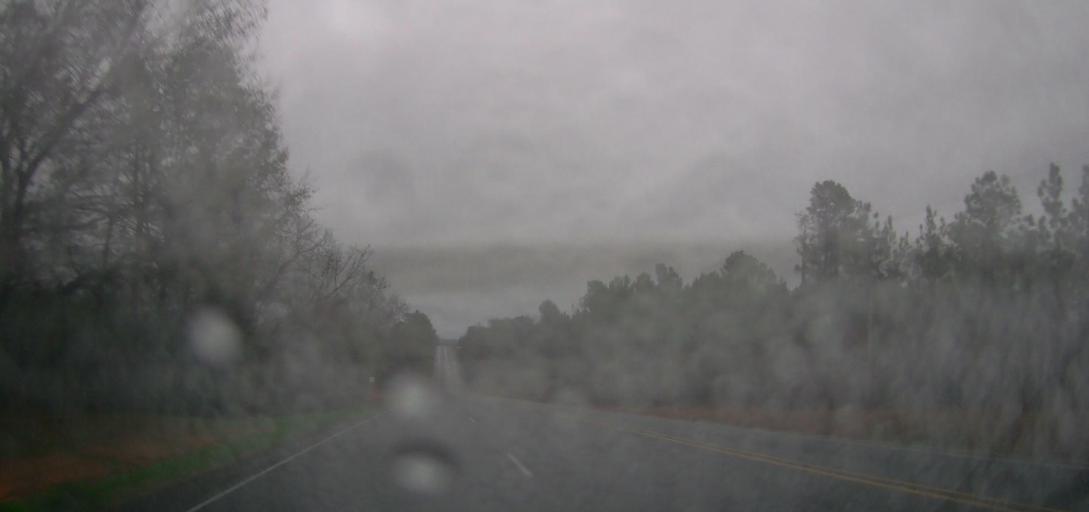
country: US
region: Alabama
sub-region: Autauga County
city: Pine Level
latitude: 32.5834
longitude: -86.6933
